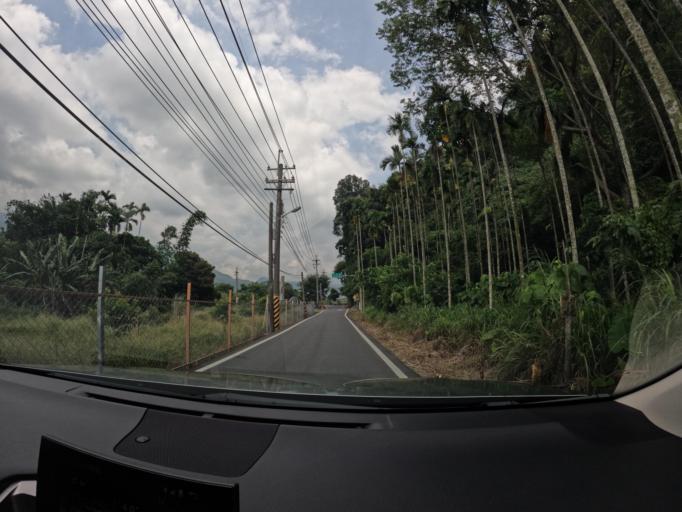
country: TW
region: Taiwan
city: Lugu
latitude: 23.8117
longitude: 120.8123
